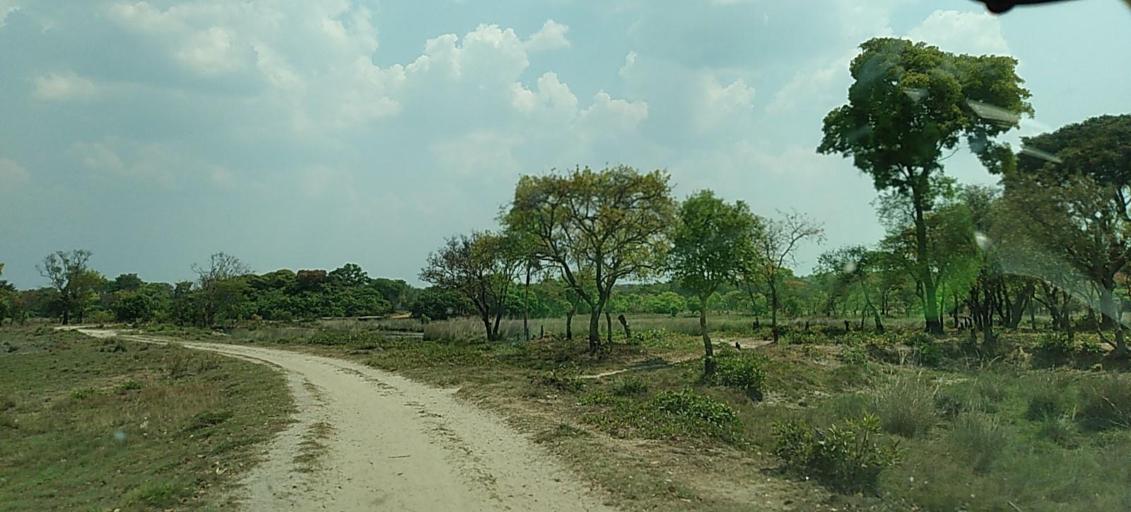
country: ZM
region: North-Western
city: Kabompo
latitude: -13.3553
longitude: 23.8950
